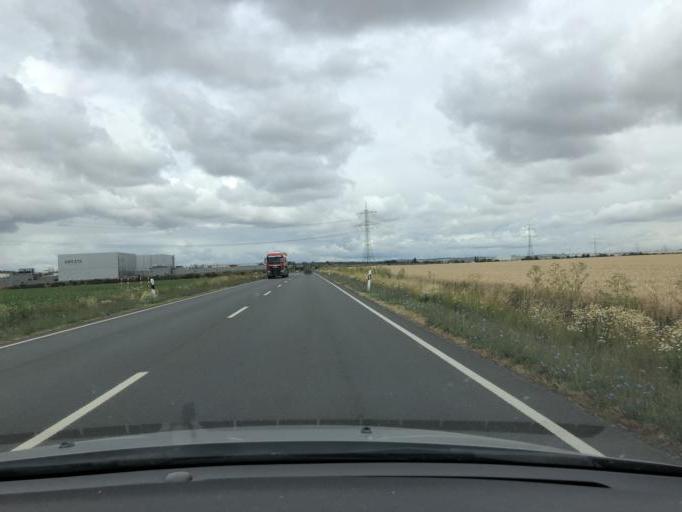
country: DE
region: Saxony-Anhalt
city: Erdeborn
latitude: 51.5039
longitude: 11.6047
